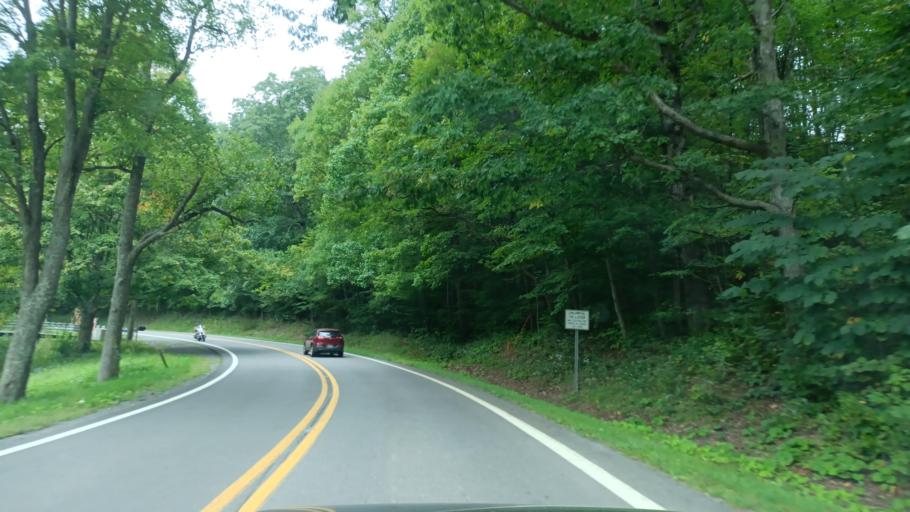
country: US
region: West Virginia
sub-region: Taylor County
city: Grafton
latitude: 39.3352
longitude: -79.8991
